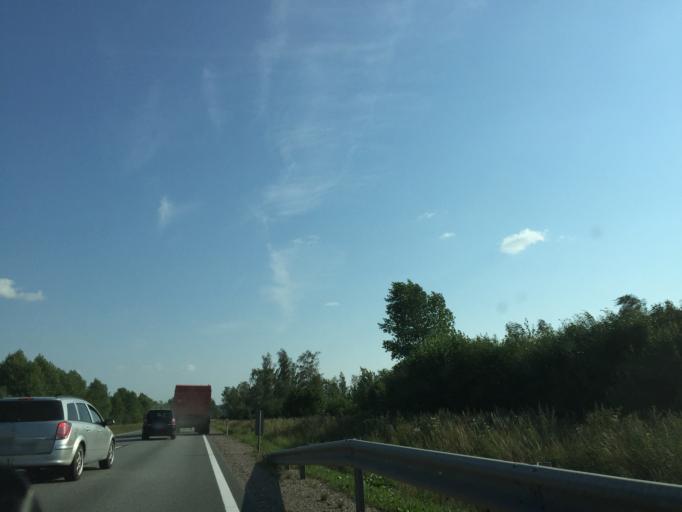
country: LT
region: Siauliu apskritis
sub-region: Joniskis
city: Joniskis
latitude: 56.4302
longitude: 23.6862
